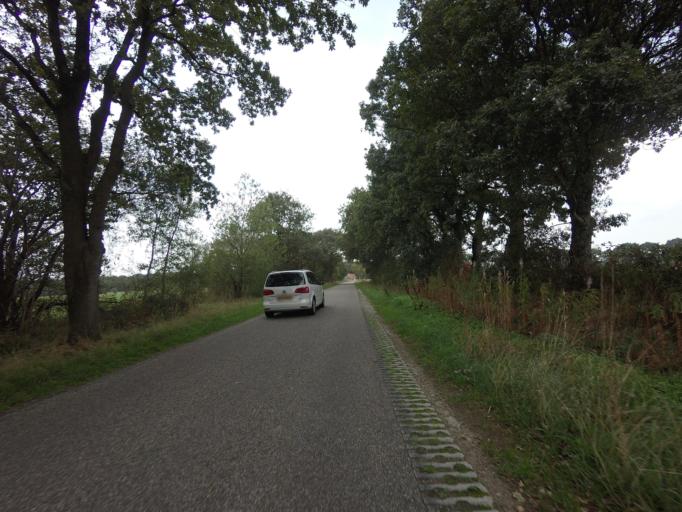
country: NL
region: Drenthe
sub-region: Gemeente Tynaarlo
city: Vries
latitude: 53.0448
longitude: 6.5944
